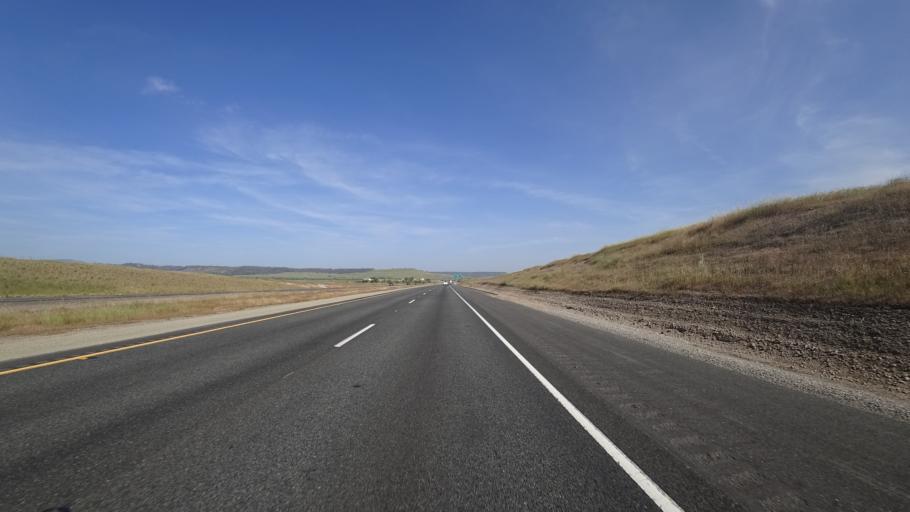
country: US
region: California
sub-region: Butte County
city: Thermalito
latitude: 39.5952
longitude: -121.6492
